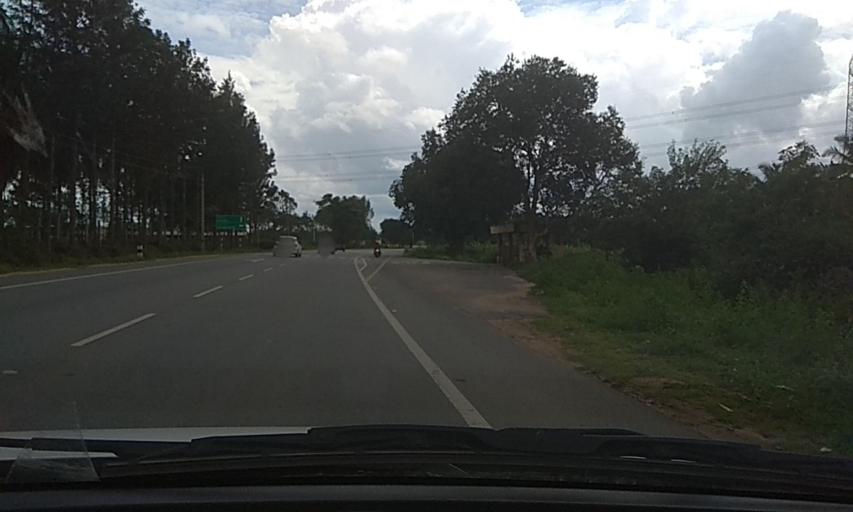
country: IN
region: Karnataka
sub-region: Tumkur
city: Tumkur
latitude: 13.2546
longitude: 77.0876
